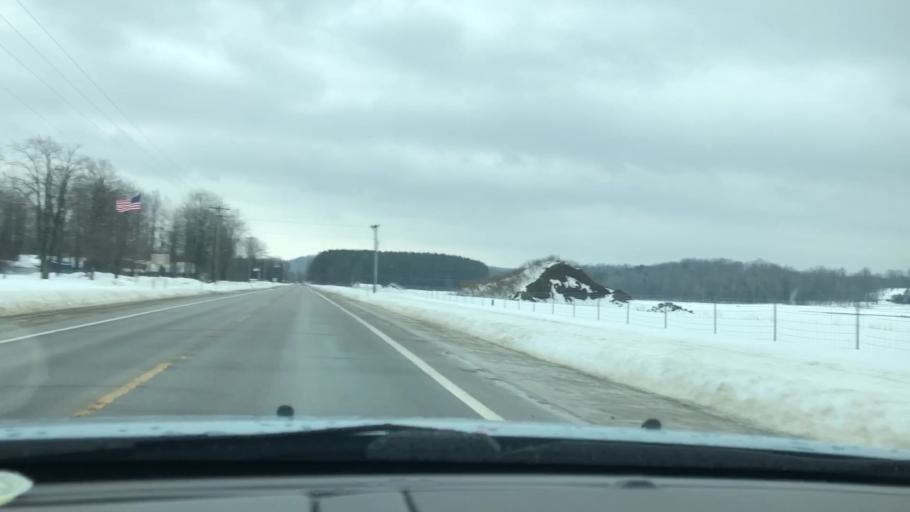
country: US
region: Michigan
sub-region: Charlevoix County
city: East Jordan
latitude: 45.1325
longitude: -85.1053
